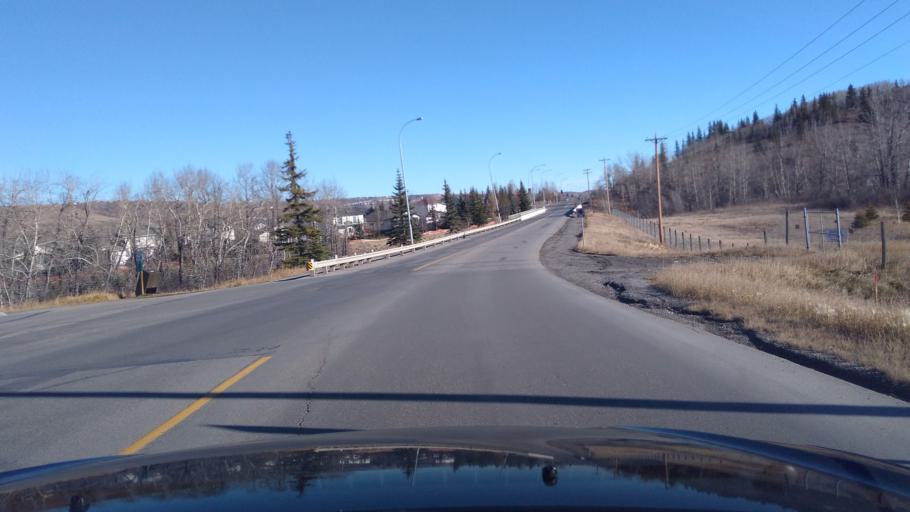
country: CA
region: Alberta
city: Cochrane
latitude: 51.1846
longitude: -114.5016
